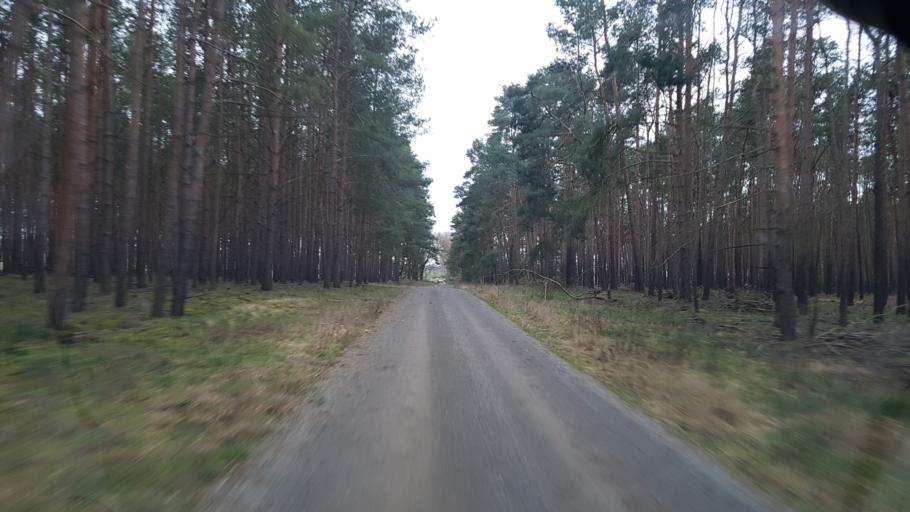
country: DE
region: Brandenburg
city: Herzberg
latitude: 51.7057
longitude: 13.2987
